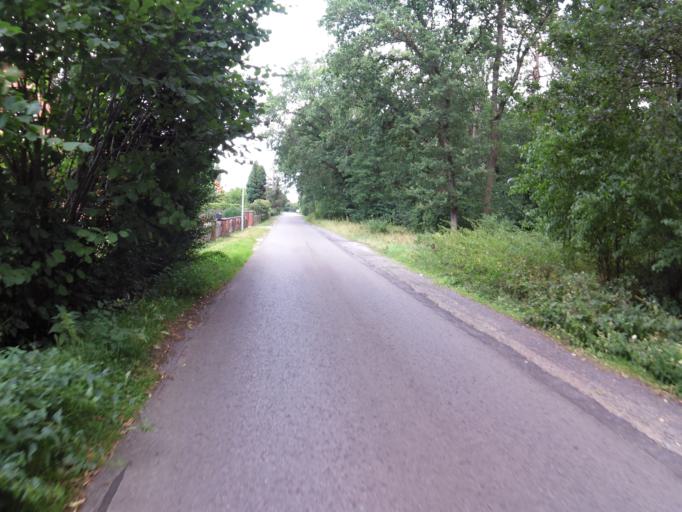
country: DE
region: Lower Saxony
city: Estorf
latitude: 52.5947
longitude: 9.1565
